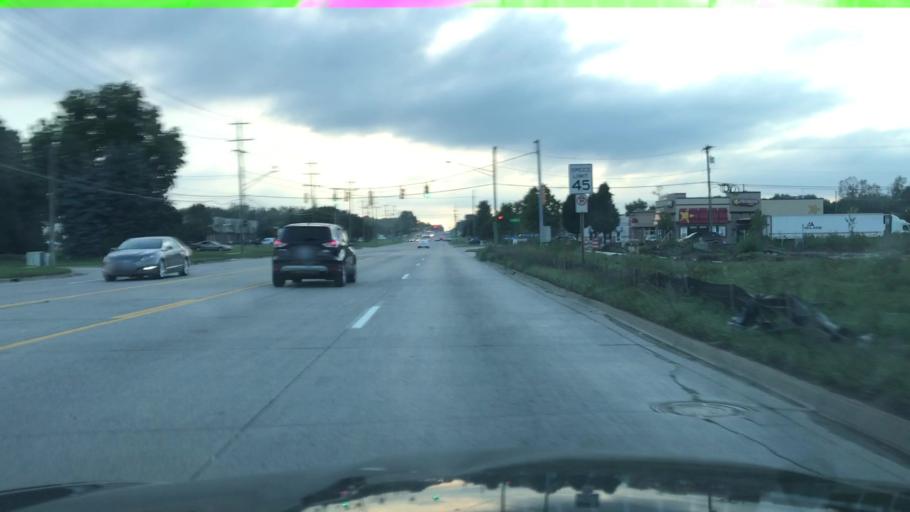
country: US
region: Michigan
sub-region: Macomb County
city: Shelby
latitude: 42.6699
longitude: -83.0061
